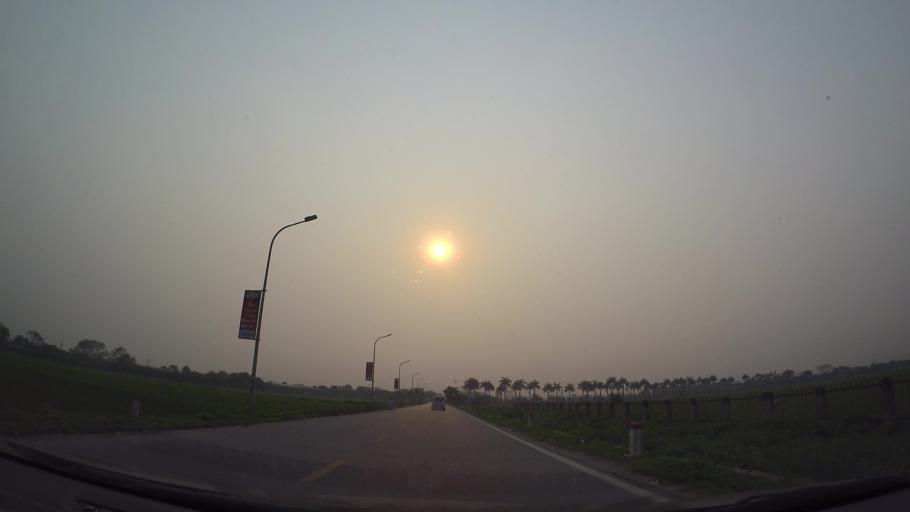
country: VN
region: Ha Noi
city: Thuong Tin
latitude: 20.8693
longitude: 105.8370
